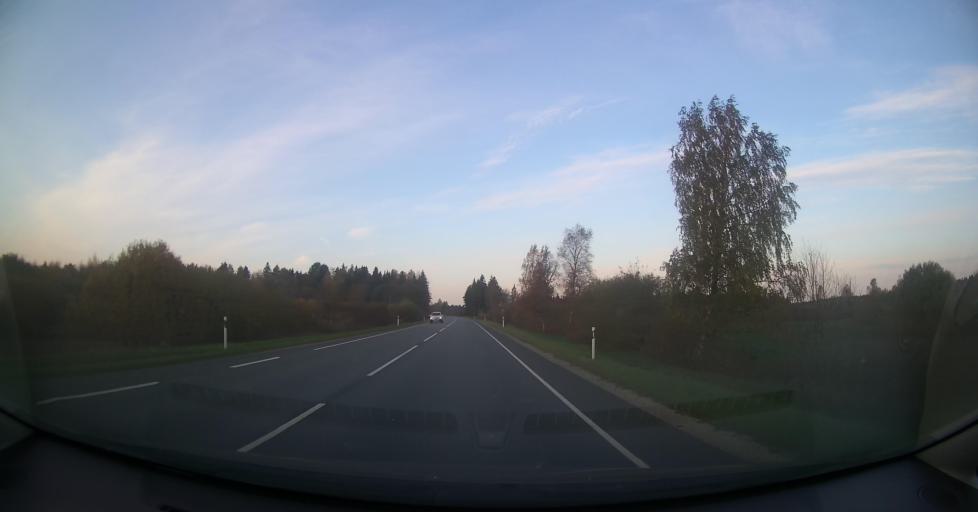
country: EE
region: Harju
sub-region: Nissi vald
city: Riisipere
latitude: 59.1190
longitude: 24.2840
